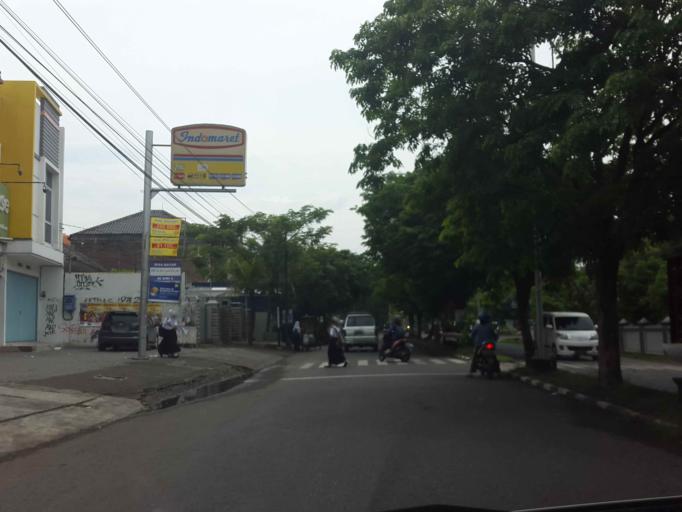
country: ID
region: Central Java
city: Semarang
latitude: -6.9951
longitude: 110.4569
